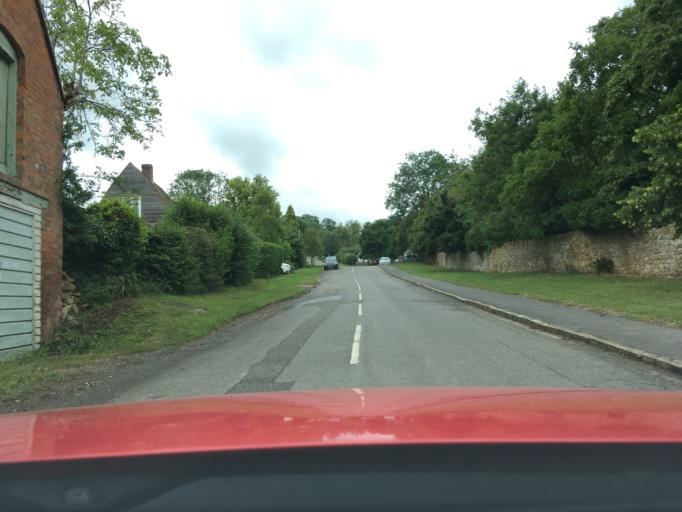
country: GB
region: England
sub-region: Warwickshire
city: Shipston on Stour
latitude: 52.0893
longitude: -1.6916
